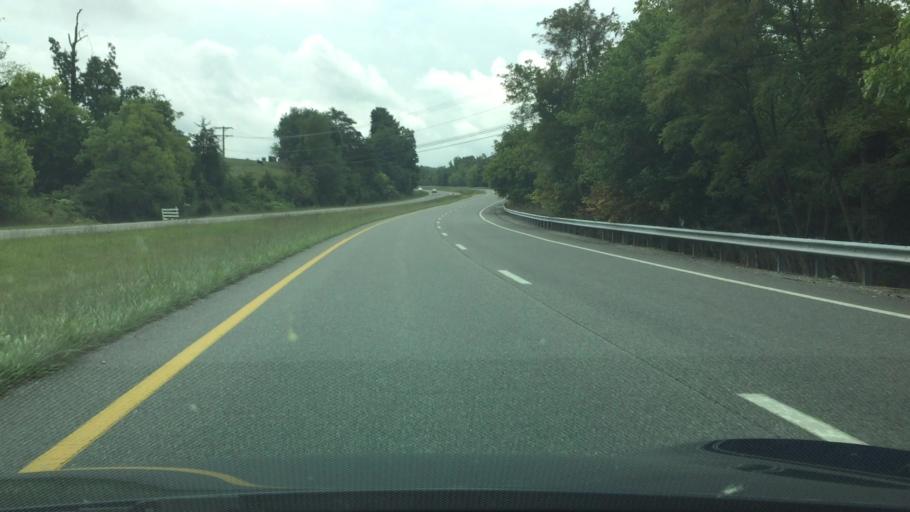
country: US
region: Virginia
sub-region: City of Radford
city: Radford
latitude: 37.1089
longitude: -80.5216
